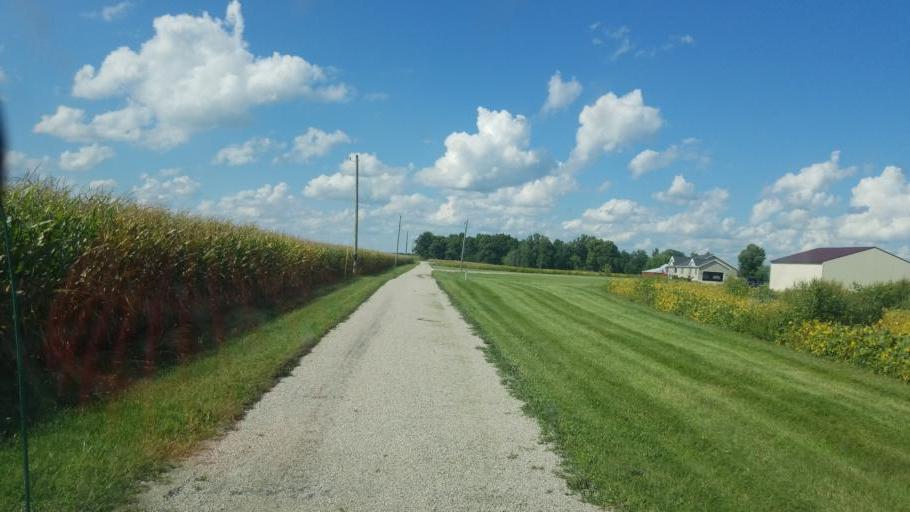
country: US
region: Ohio
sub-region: Union County
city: Richwood
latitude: 40.5100
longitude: -83.3704
